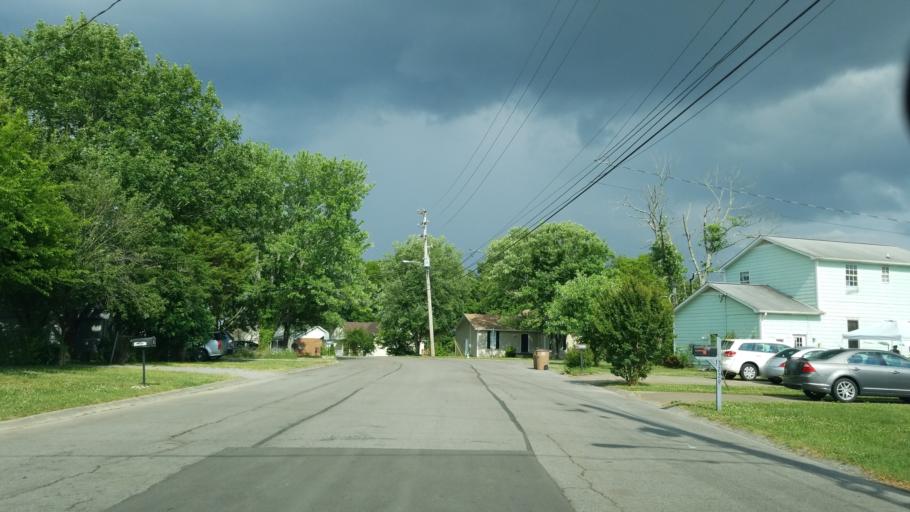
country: US
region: Tennessee
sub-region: Rutherford County
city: La Vergne
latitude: 36.0697
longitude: -86.6041
